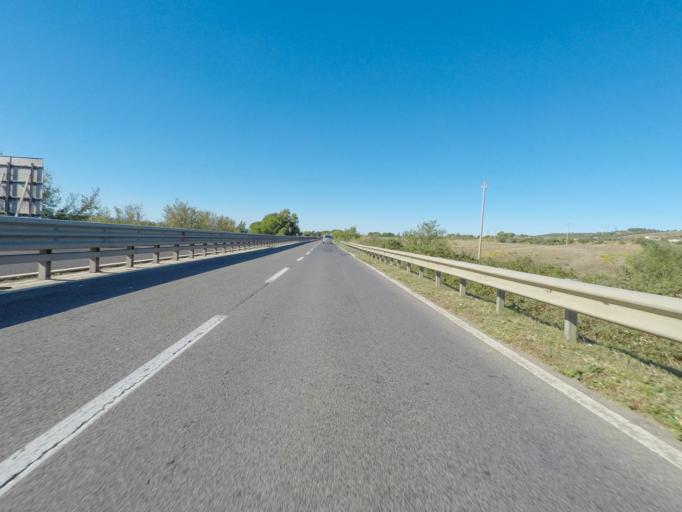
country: IT
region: Tuscany
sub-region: Provincia di Grosseto
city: Grosseto
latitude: 42.7188
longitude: 11.1410
